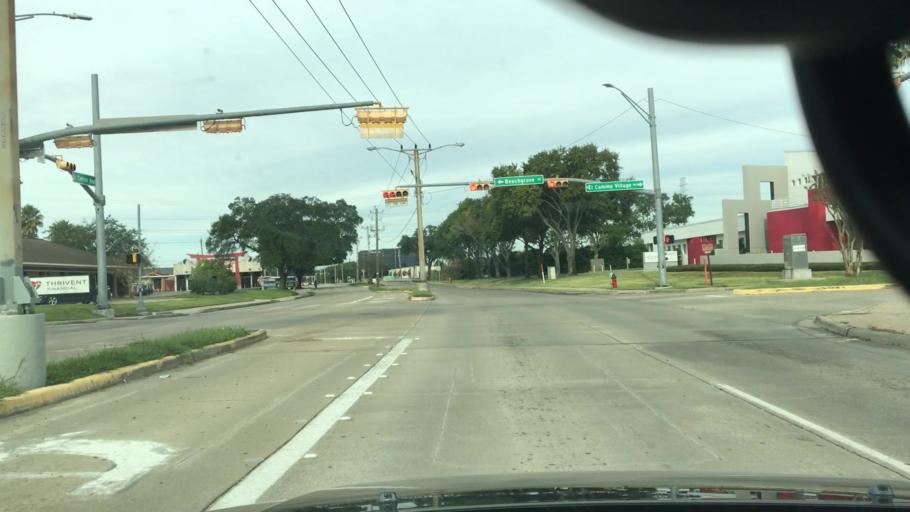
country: US
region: Texas
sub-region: Harris County
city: Webster
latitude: 29.5495
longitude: -95.1098
